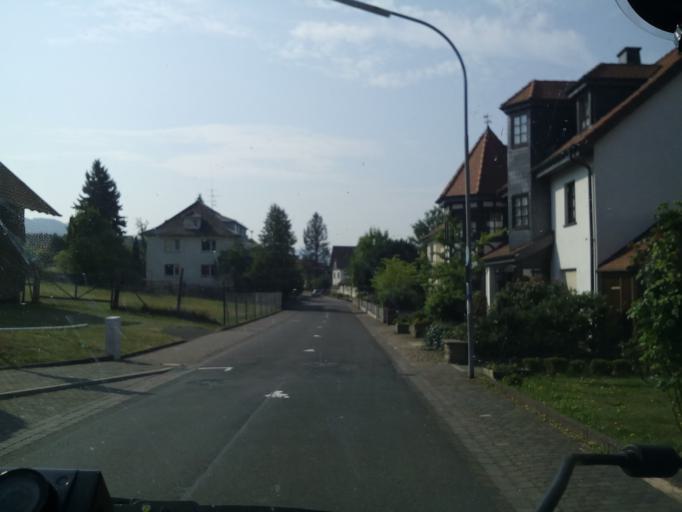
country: DE
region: Hesse
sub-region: Regierungsbezirk Kassel
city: Hilders
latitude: 50.5741
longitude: 10.0009
